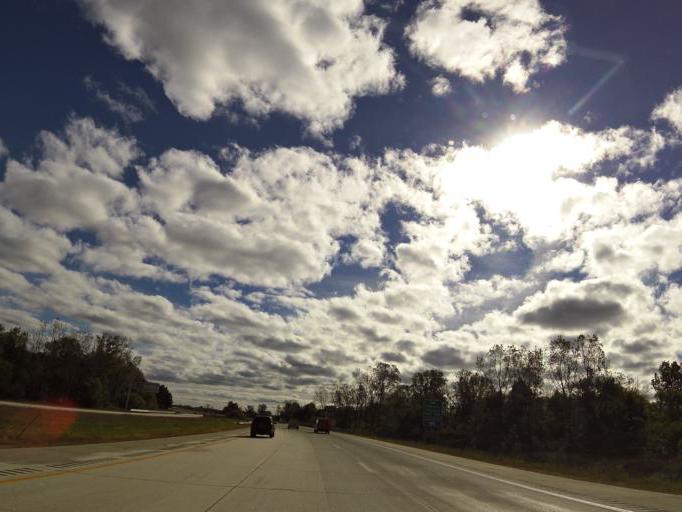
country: US
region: Michigan
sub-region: Genesee County
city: Burton
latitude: 43.0164
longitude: -83.5712
